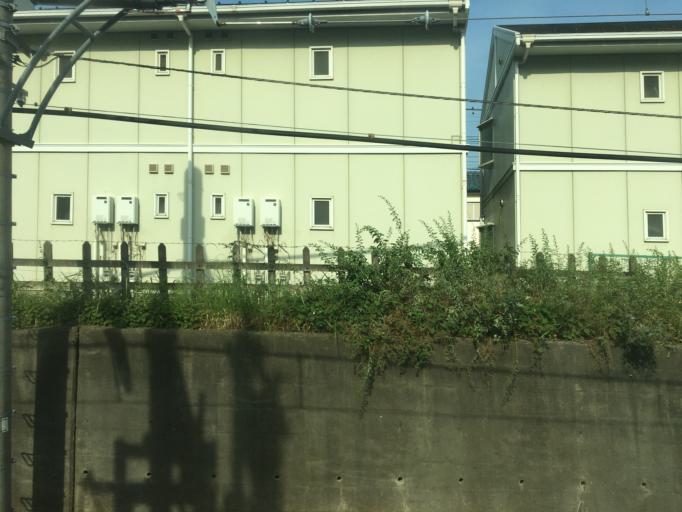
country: JP
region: Saitama
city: Tokorozawa
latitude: 35.7907
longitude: 139.4734
